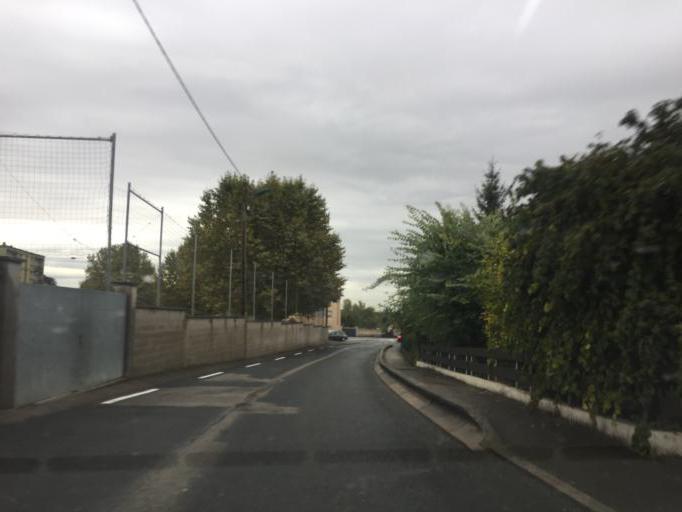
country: FR
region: Rhone-Alpes
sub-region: Departement de l'Ain
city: Miribel
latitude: 45.8217
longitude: 4.9444
